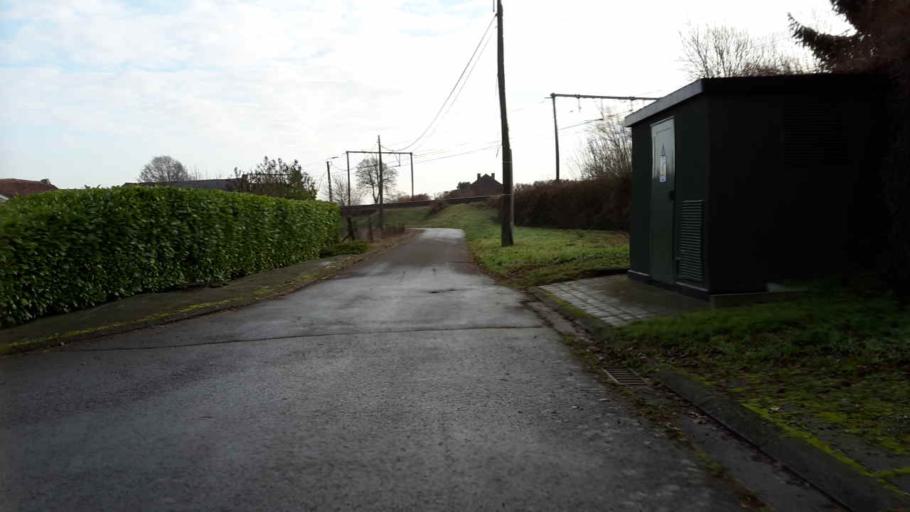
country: BE
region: Flanders
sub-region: Provincie Vlaams-Brabant
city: Hoegaarden
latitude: 50.8157
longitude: 4.8935
